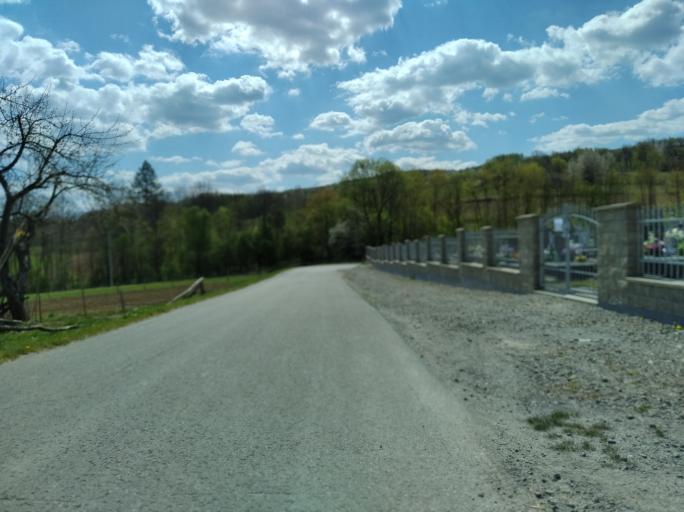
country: PL
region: Subcarpathian Voivodeship
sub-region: Powiat brzozowski
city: Wesola
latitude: 49.7765
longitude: 22.1312
